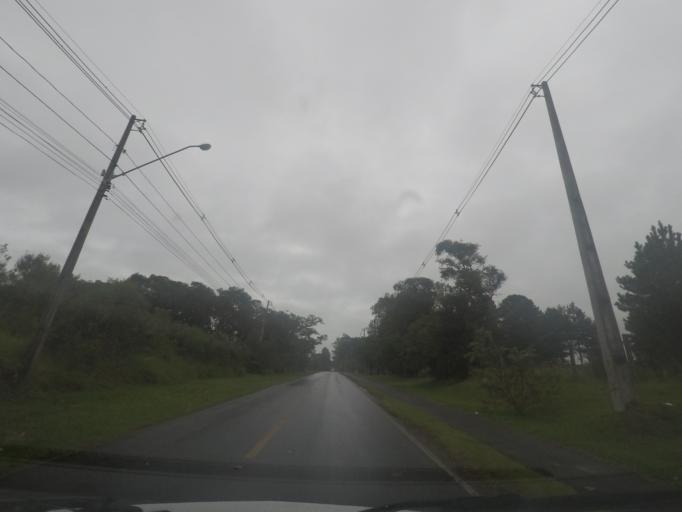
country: BR
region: Parana
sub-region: Quatro Barras
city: Quatro Barras
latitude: -25.3723
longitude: -49.0880
